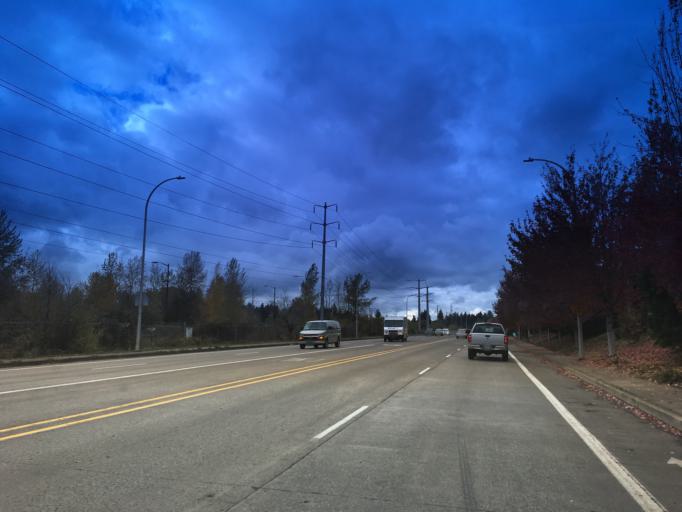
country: US
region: Oregon
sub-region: Multnomah County
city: Fairview
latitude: 45.5280
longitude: -122.4428
